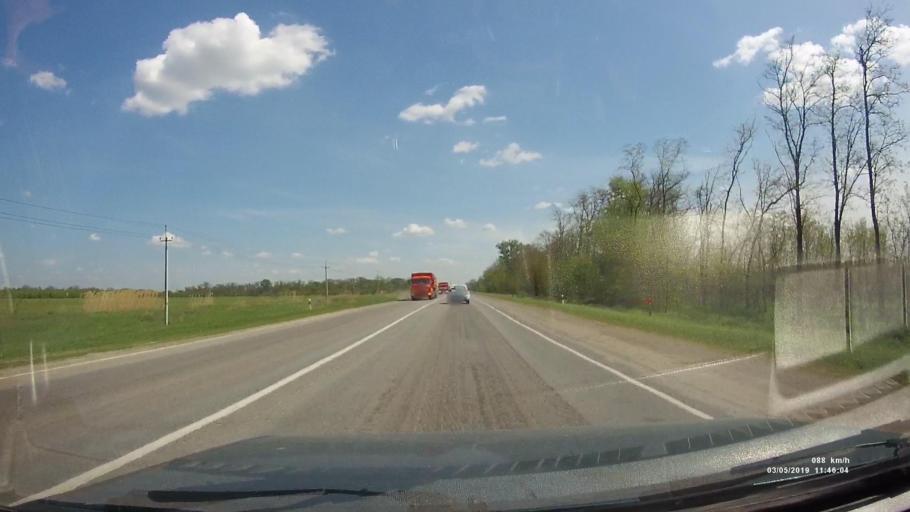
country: RU
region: Rostov
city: Starocherkasskaya
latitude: 47.1479
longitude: 40.1119
